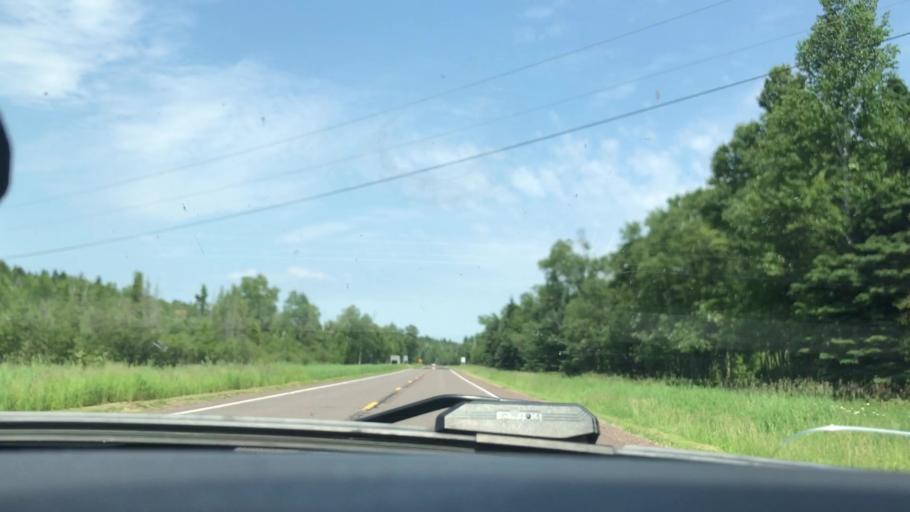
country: US
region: Minnesota
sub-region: Lake County
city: Silver Bay
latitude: 47.4891
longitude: -90.9850
